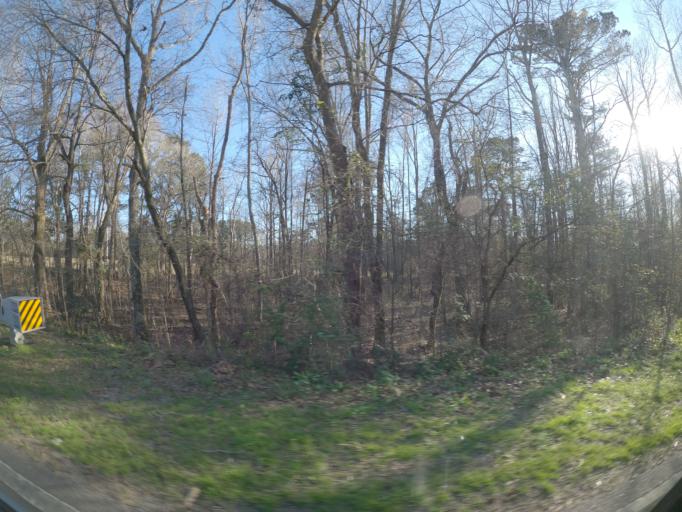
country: US
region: Georgia
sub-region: Columbia County
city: Grovetown
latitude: 33.4517
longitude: -82.2171
